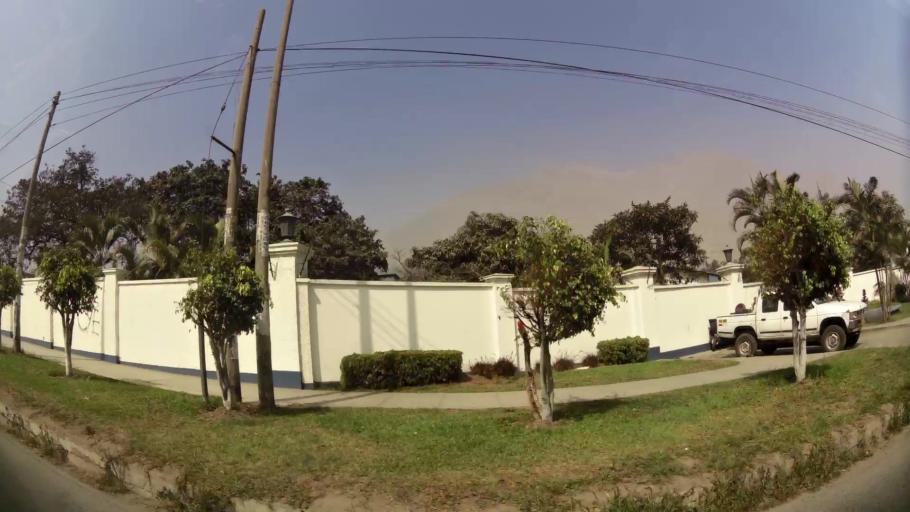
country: PE
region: Lima
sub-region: Lima
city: Asentamiento Humano Nicolas de Pierola
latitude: -11.9278
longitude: -76.6887
